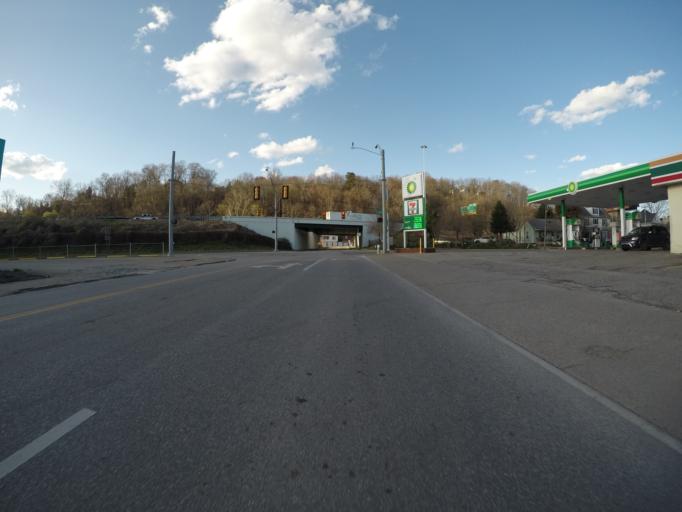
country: US
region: West Virginia
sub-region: Kanawha County
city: Charleston
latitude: 38.3604
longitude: -81.6274
